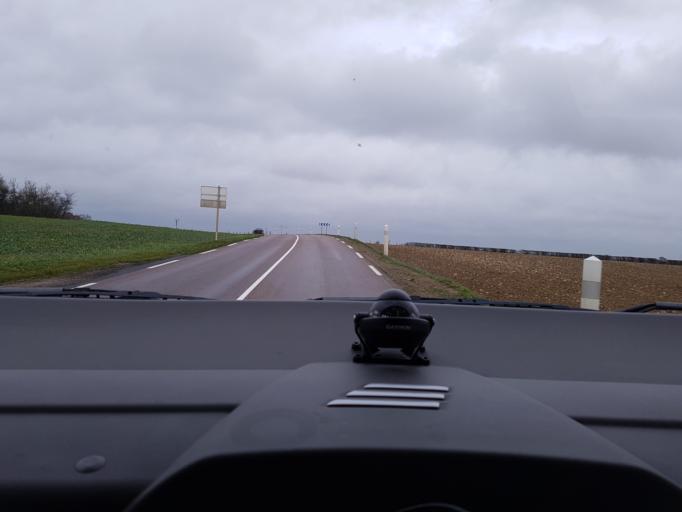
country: FR
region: Picardie
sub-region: Departement de l'Oise
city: Songeons
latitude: 49.5142
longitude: 1.8196
